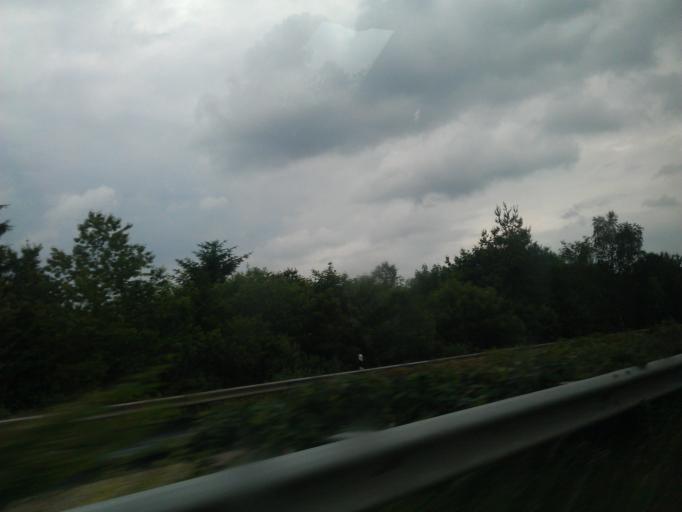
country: DE
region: Rheinland-Pfalz
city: Hinzert-Polert
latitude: 49.6800
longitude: 6.9105
